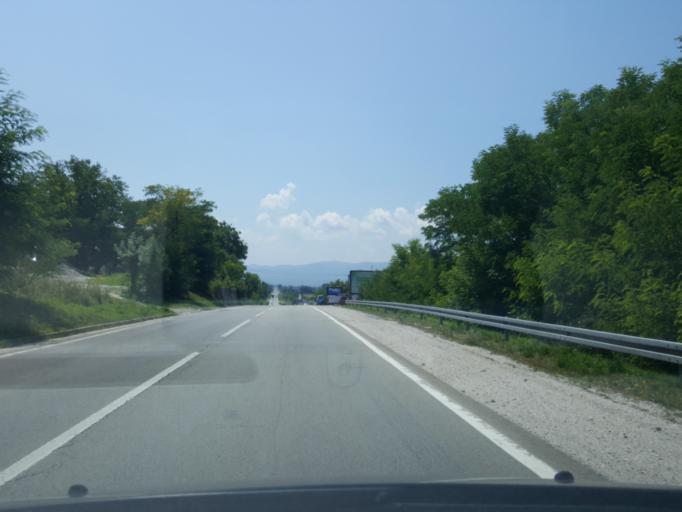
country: RS
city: Prislonica
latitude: 43.9518
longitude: 20.4155
